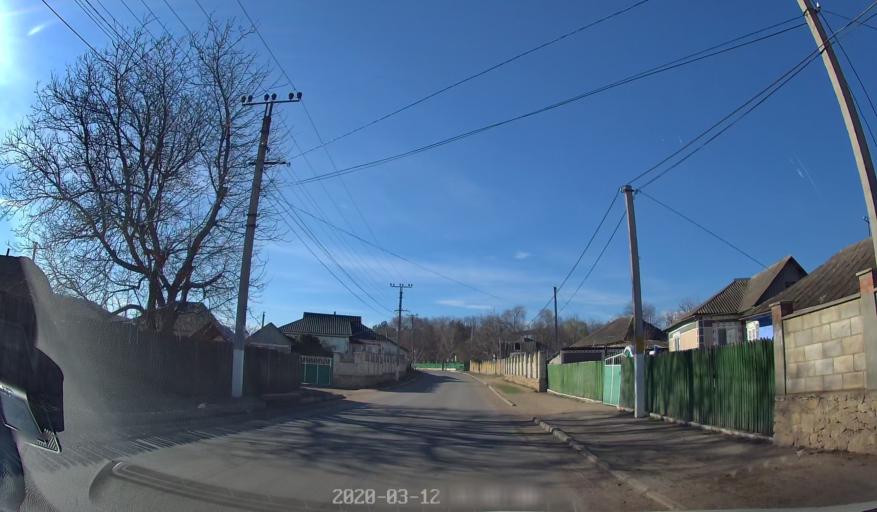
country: MD
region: Telenesti
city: Cocieri
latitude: 47.2204
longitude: 29.0059
